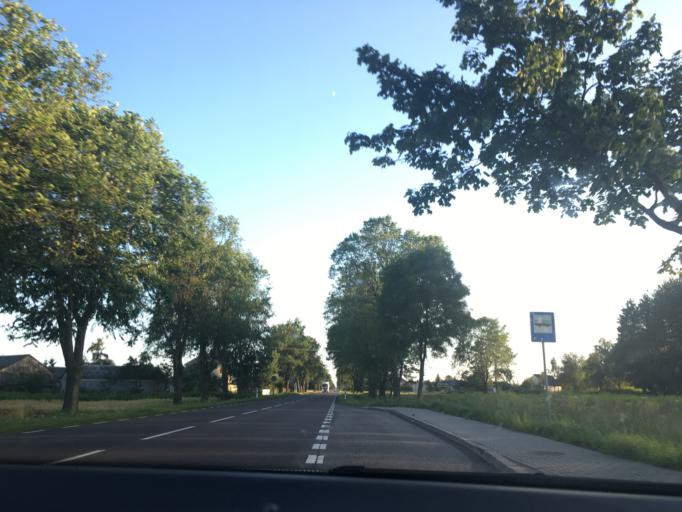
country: PL
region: Lublin Voivodeship
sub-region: Powiat bialski
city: Rzeczyca
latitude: 51.9313
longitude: 22.7169
